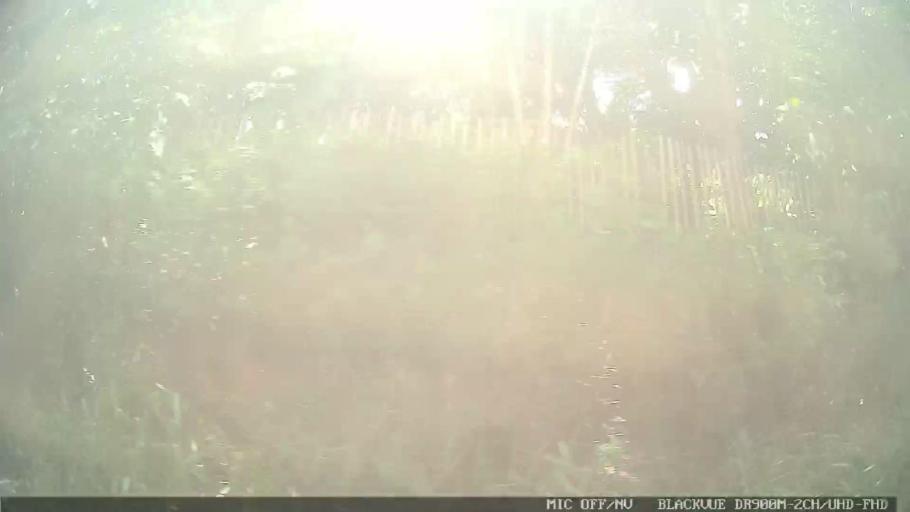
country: BR
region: Sao Paulo
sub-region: Braganca Paulista
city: Braganca Paulista
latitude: -23.0304
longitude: -46.5321
